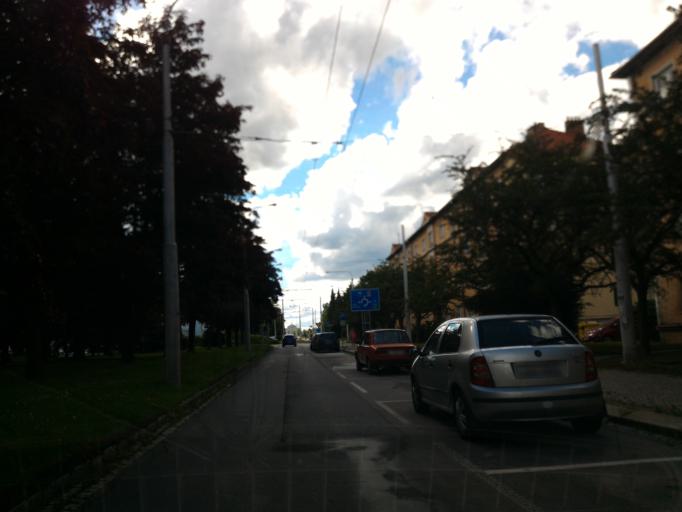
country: CZ
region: Vysocina
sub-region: Okres Jihlava
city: Jihlava
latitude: 49.3970
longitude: 15.5756
